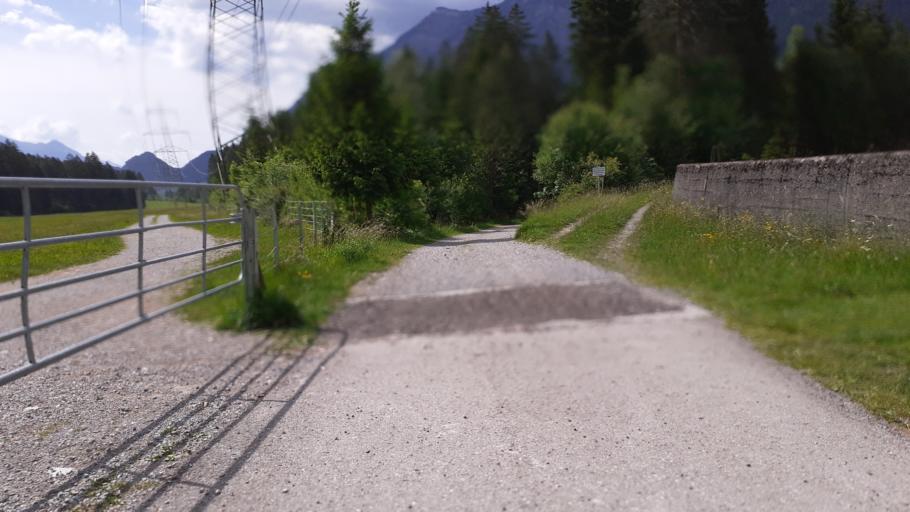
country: AT
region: Vorarlberg
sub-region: Politischer Bezirk Bludenz
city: Innerbraz
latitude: 47.1387
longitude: 9.9243
